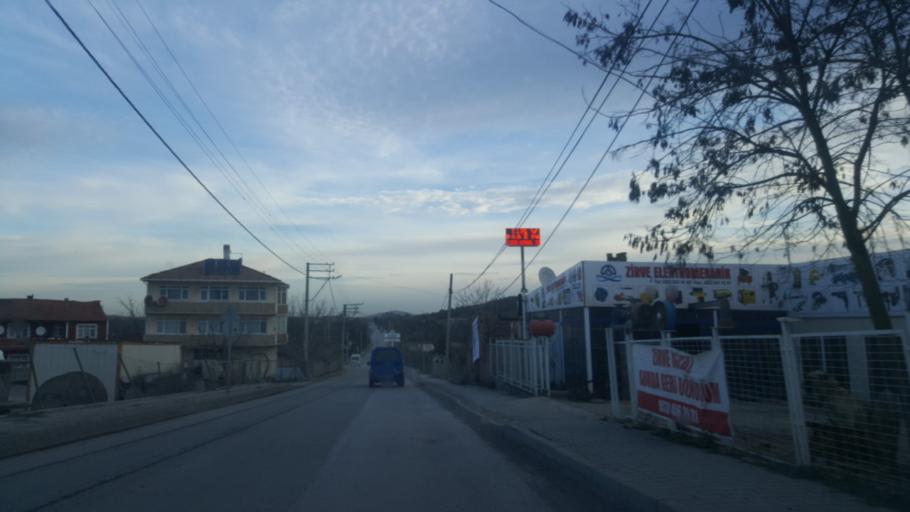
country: TR
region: Kocaeli
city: Tavsanli
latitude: 40.8481
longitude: 29.5549
